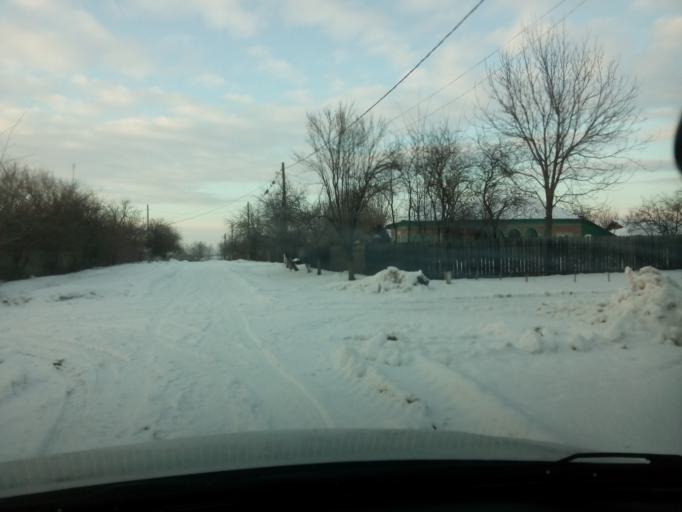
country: RO
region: Calarasi
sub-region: Comuna Luica
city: Luica
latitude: 44.2475
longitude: 26.6121
